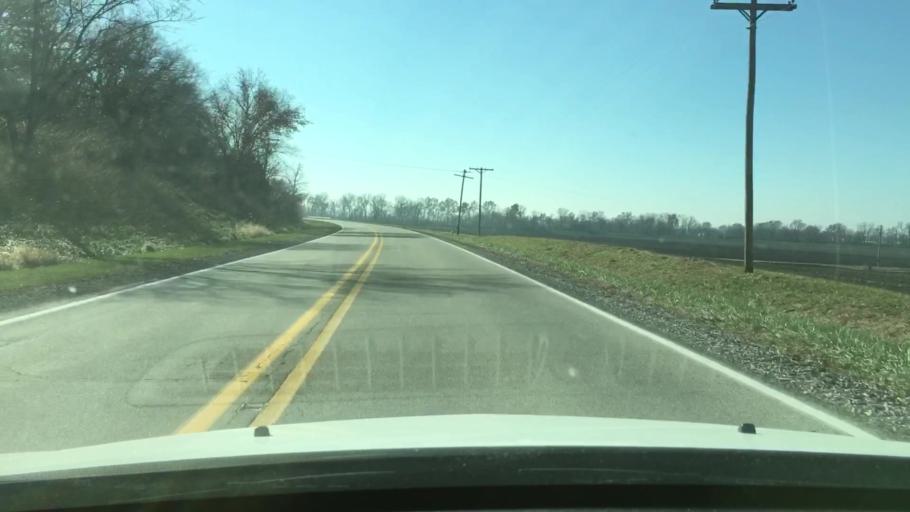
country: US
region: Illinois
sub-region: Morgan County
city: Meredosia
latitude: 39.7259
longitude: -90.5672
